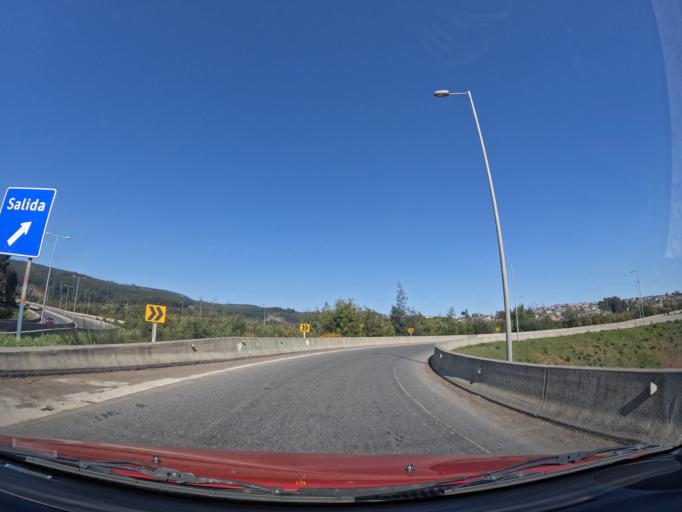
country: CL
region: Biobio
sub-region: Provincia de Concepcion
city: Lota
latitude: -37.0719
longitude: -73.1447
